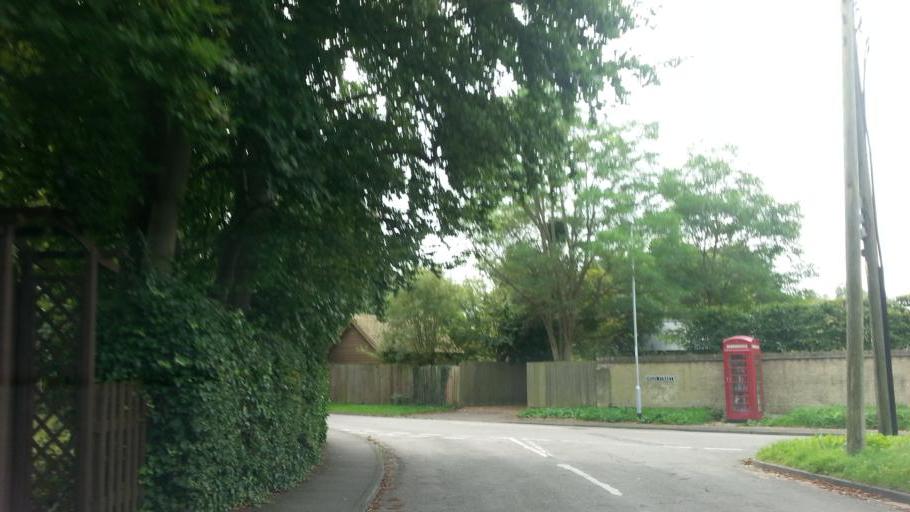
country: GB
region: England
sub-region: Cambridgeshire
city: Barton
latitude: 52.1823
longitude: 0.0560
